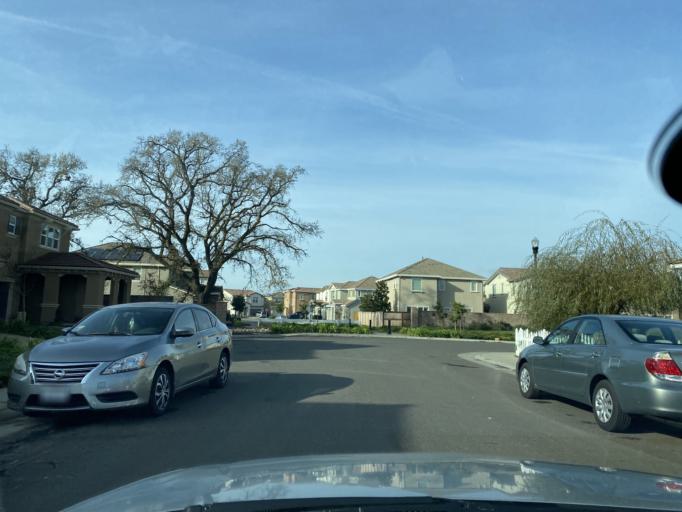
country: US
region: California
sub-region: Sacramento County
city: Elk Grove
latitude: 38.3994
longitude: -121.3895
